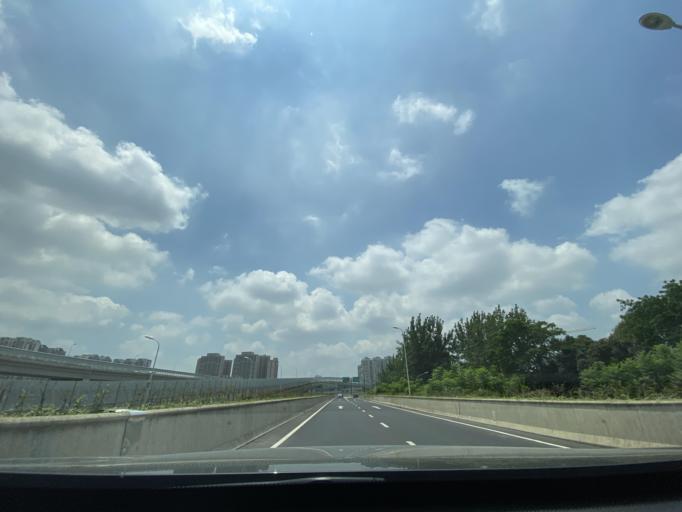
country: CN
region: Sichuan
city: Chengdu
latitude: 30.5991
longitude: 104.1103
